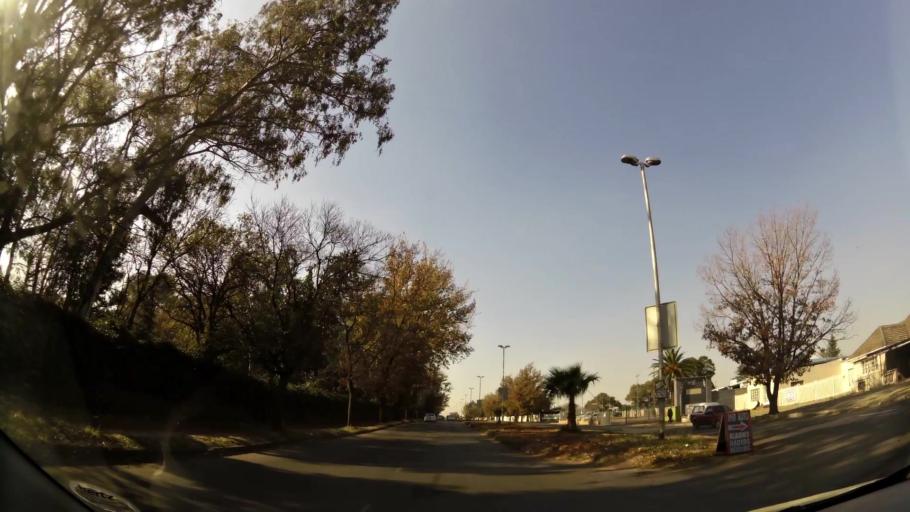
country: ZA
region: Gauteng
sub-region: West Rand District Municipality
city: Randfontein
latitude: -26.1733
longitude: 27.6961
